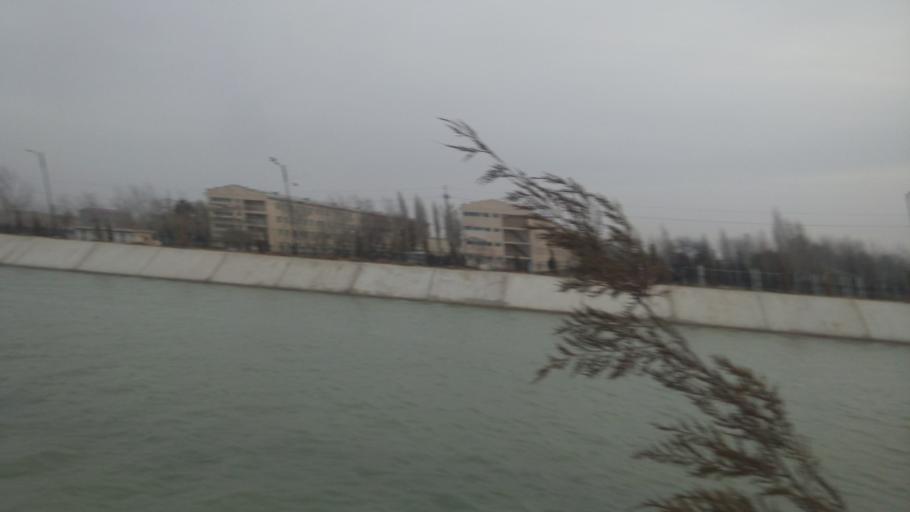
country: UZ
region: Sirdaryo
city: Guliston
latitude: 40.5054
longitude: 68.7809
